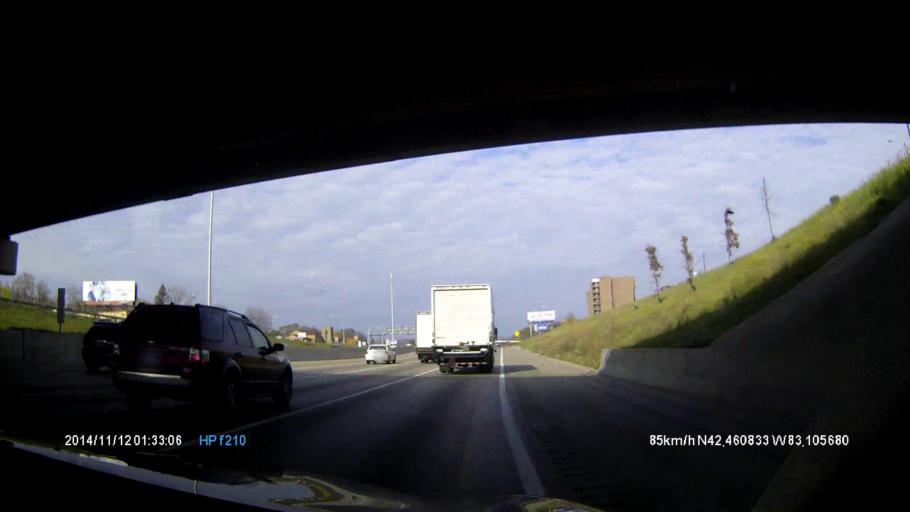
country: US
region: Michigan
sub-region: Oakland County
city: Hazel Park
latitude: 42.4610
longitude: -83.1057
